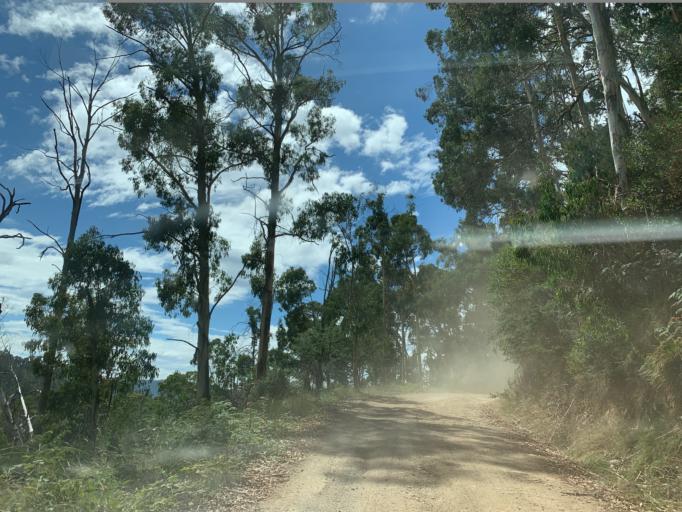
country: AU
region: Victoria
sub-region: Mansfield
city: Mansfield
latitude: -37.1001
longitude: 146.5043
